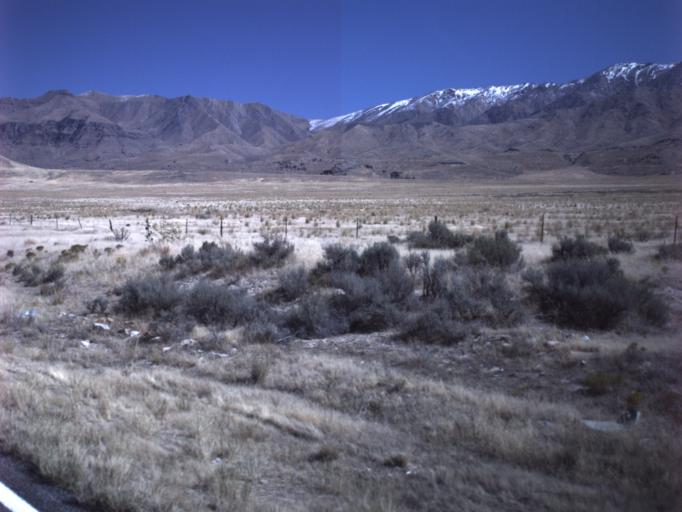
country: US
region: Utah
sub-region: Tooele County
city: Grantsville
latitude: 40.6018
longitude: -112.7124
